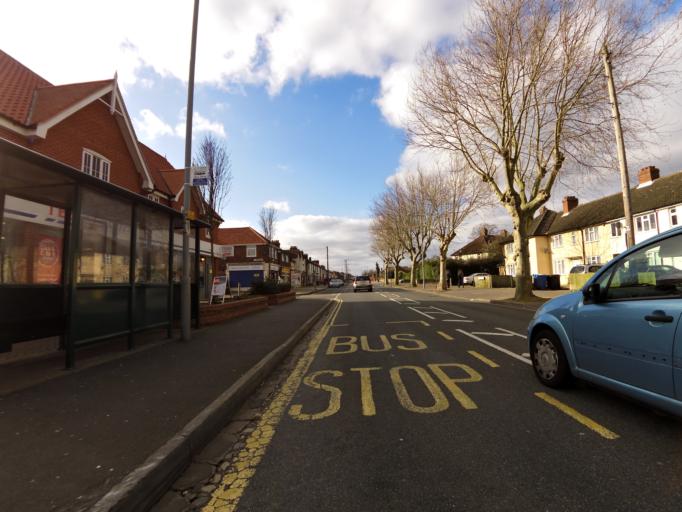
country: GB
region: England
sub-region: Suffolk
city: Ipswich
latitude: 52.0400
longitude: 1.1860
